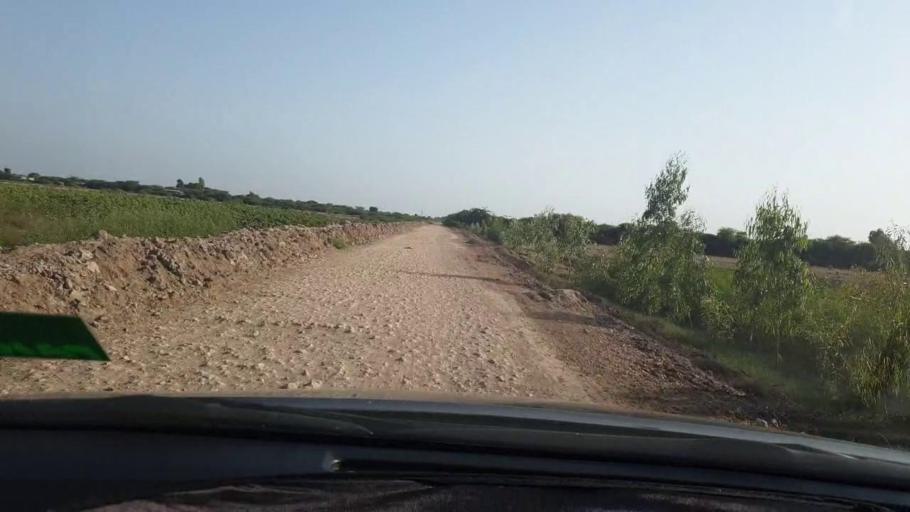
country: PK
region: Sindh
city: Naukot
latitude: 24.9074
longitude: 69.2765
